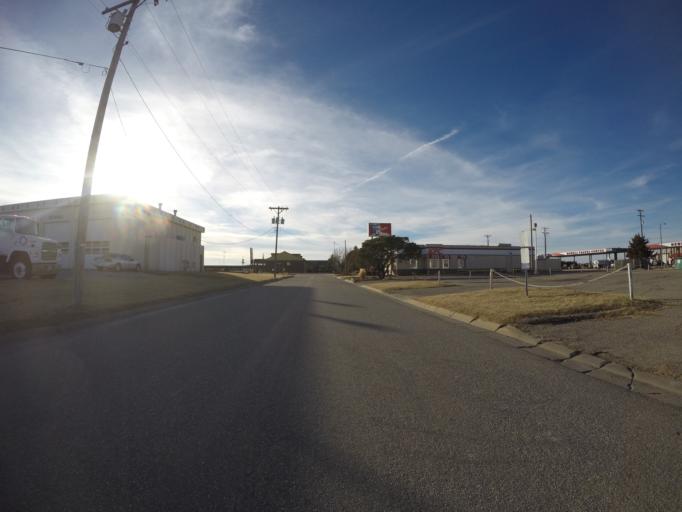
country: US
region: Kansas
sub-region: Harvey County
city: Newton
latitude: 38.0434
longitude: -97.3194
